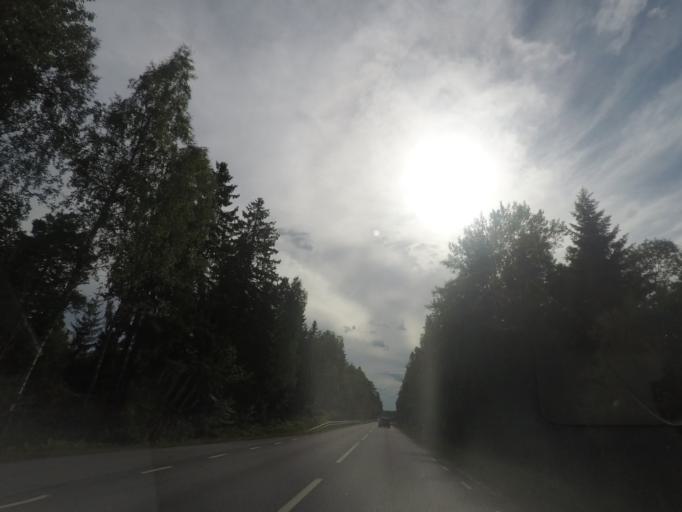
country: SE
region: Stockholm
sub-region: Norrtalje Kommun
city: Skanninge
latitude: 59.9044
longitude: 18.5782
